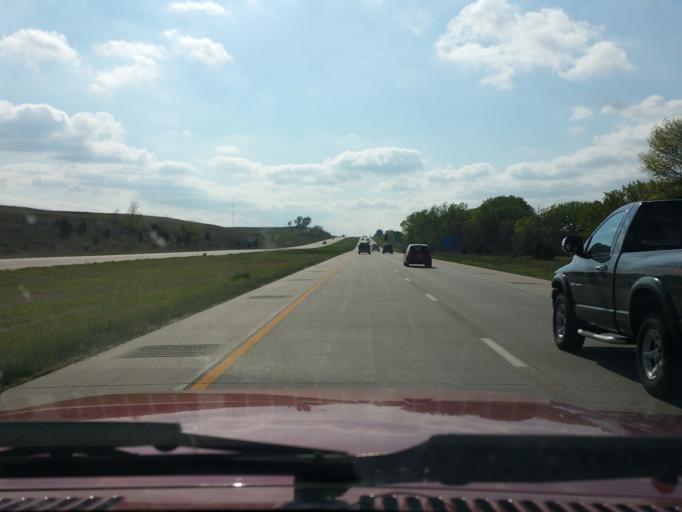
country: US
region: Kansas
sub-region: Wabaunsee County
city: Alma
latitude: 39.0657
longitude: -96.2717
